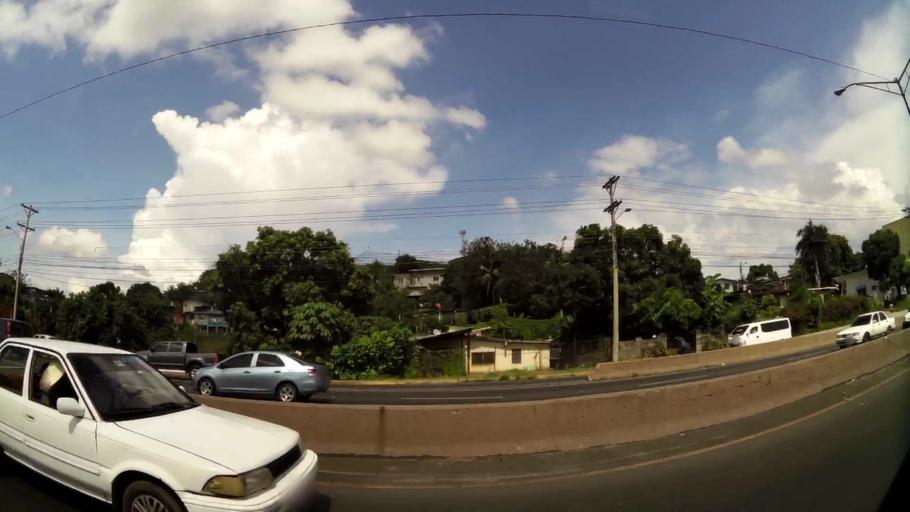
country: PA
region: Panama
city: San Miguelito
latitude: 9.0300
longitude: -79.4924
